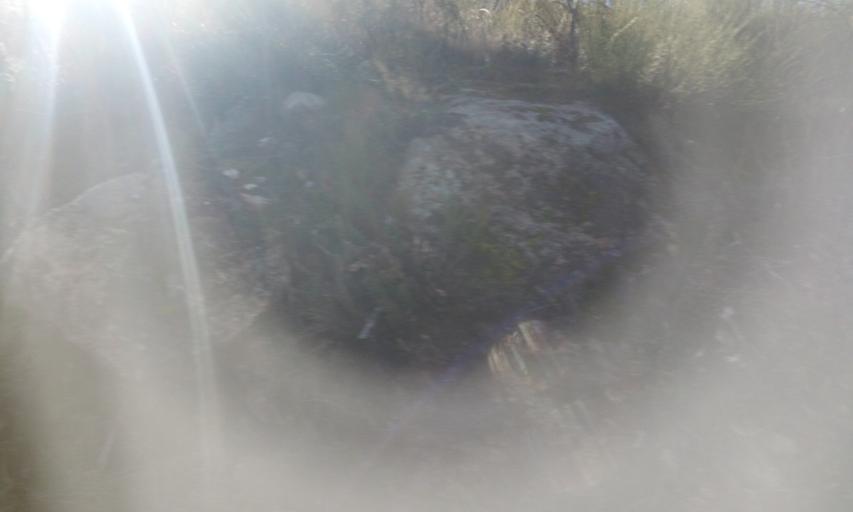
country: PT
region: Guarda
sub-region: Manteigas
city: Manteigas
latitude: 40.4854
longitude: -7.5181
